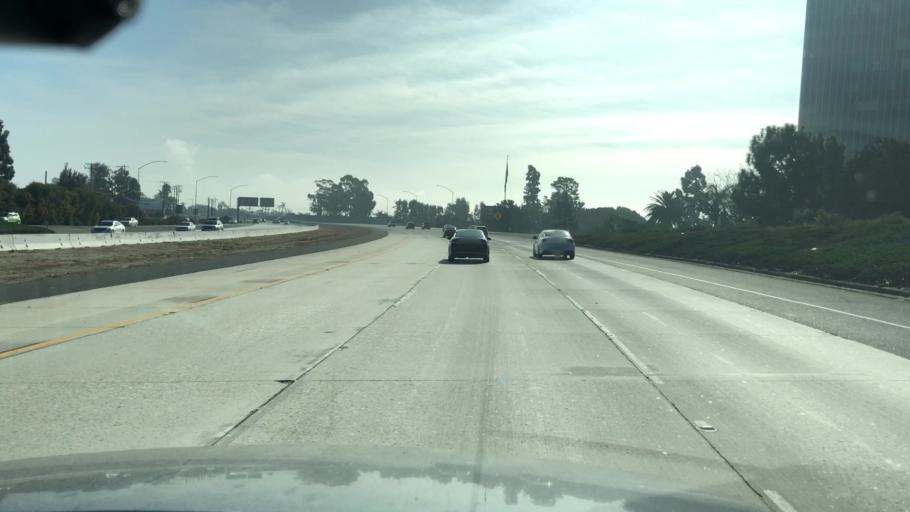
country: US
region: California
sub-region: Ventura County
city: El Rio
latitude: 34.2306
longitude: -119.1724
